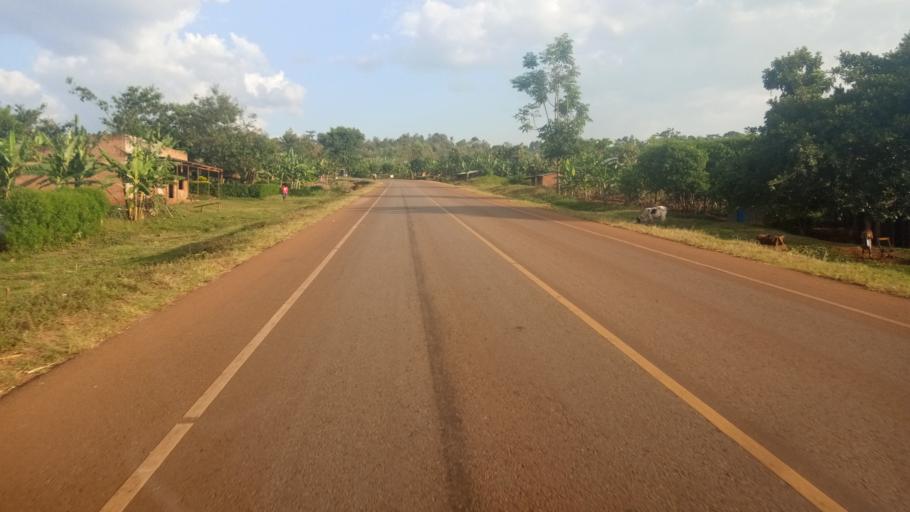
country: UG
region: Eastern Region
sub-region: Sironko District
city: Sironko
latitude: 1.3299
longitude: 34.3252
